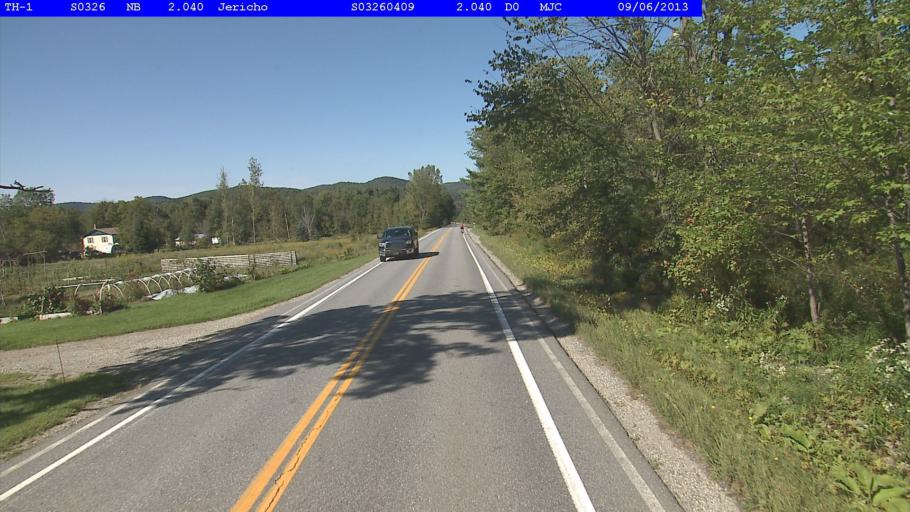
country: US
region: Vermont
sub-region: Chittenden County
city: Jericho
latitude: 44.5059
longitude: -72.9541
